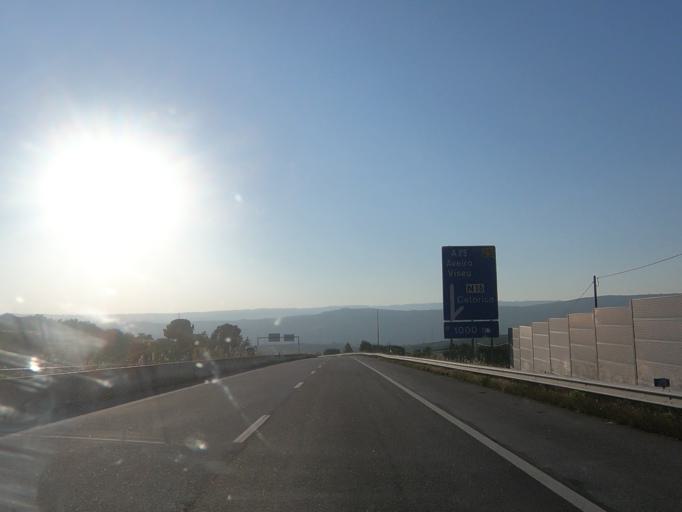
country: PT
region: Guarda
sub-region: Celorico da Beira
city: Celorico da Beira
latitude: 40.6265
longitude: -7.4043
